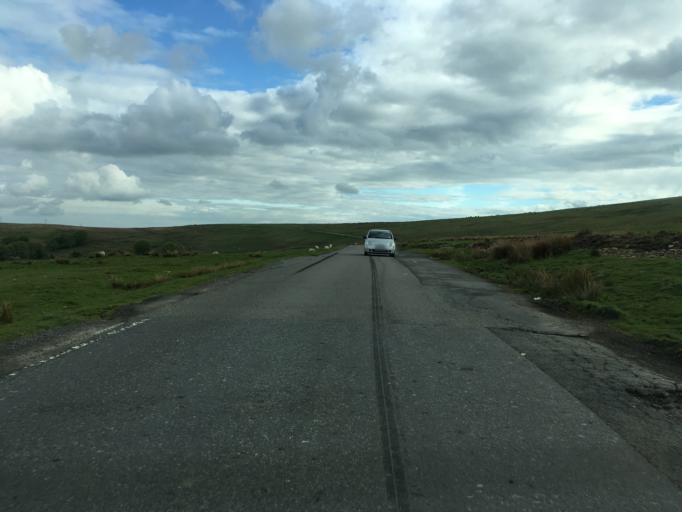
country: GB
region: Wales
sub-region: Caerphilly County Borough
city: Rhymney
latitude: 51.7275
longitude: -3.2972
